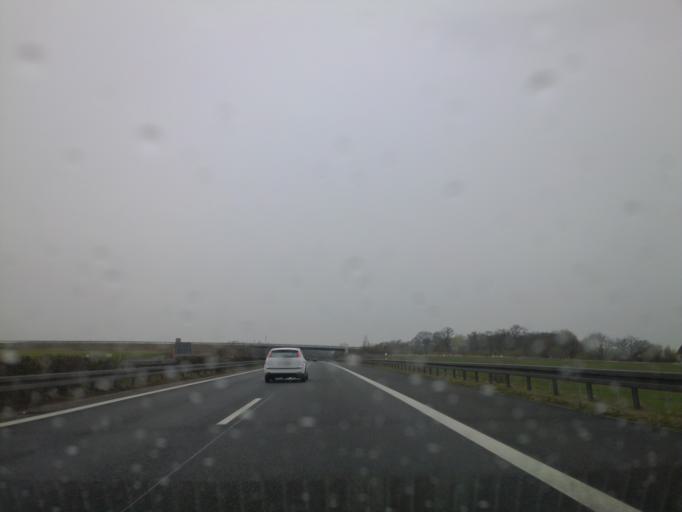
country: DE
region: Mecklenburg-Vorpommern
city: Broderstorf
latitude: 54.0403
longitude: 12.3493
